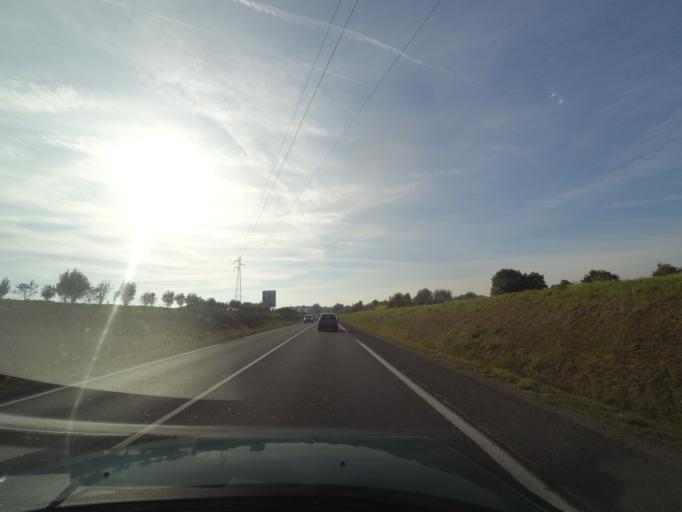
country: FR
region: Pays de la Loire
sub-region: Departement de la Vendee
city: Bouffere
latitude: 46.9675
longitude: -1.3289
